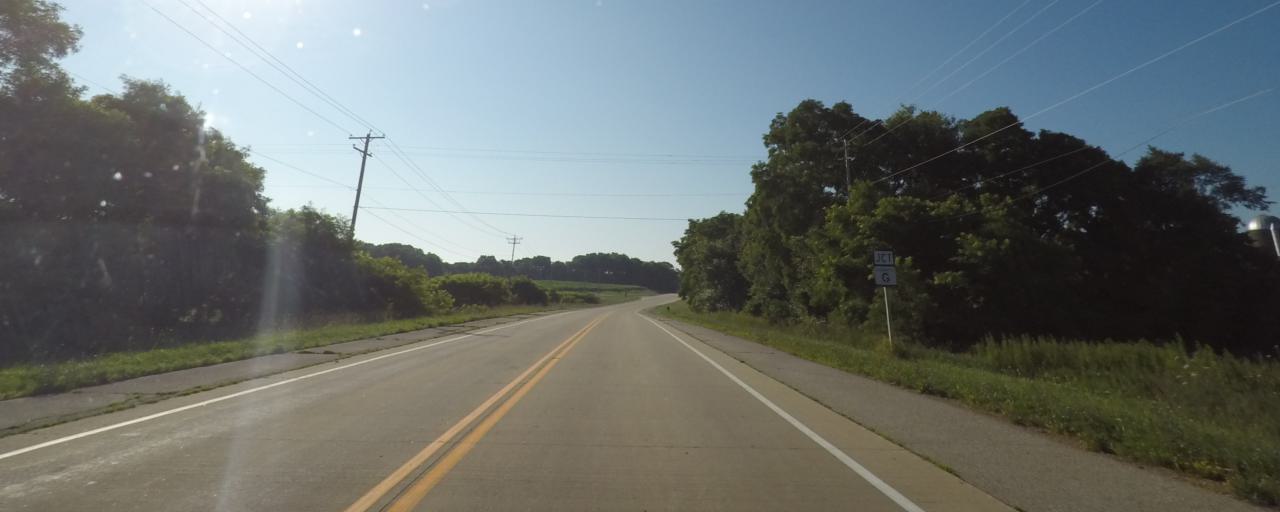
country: US
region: Wisconsin
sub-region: Jefferson County
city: Lake Koshkonong
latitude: 42.9608
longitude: -88.8948
